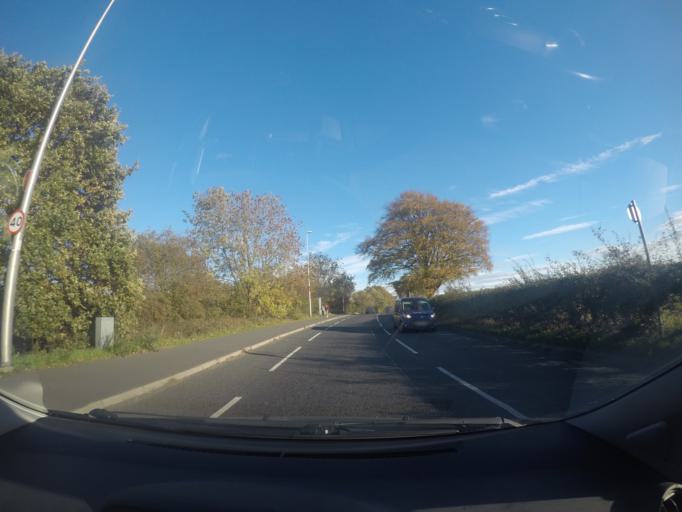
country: GB
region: England
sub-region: City of York
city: Nether Poppleton
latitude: 53.9720
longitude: -1.1394
